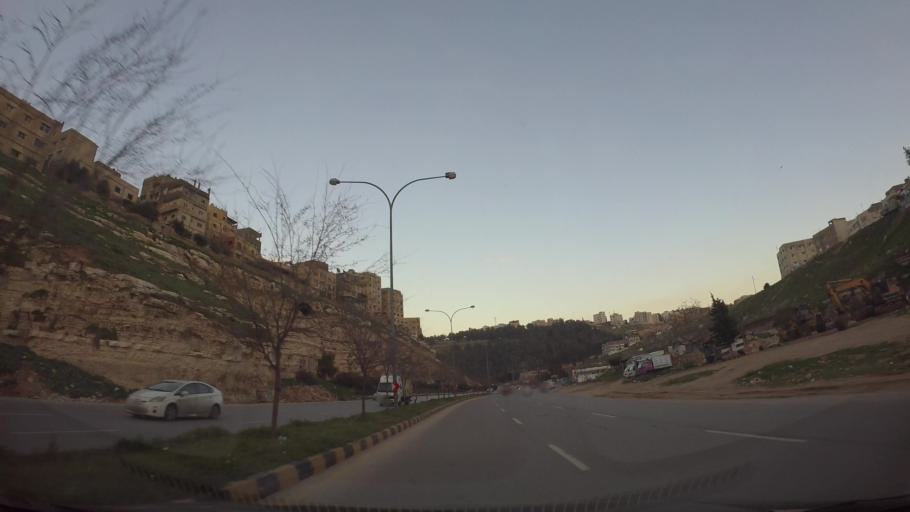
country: JO
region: Amman
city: Al Quwaysimah
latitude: 31.9275
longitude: 35.9142
